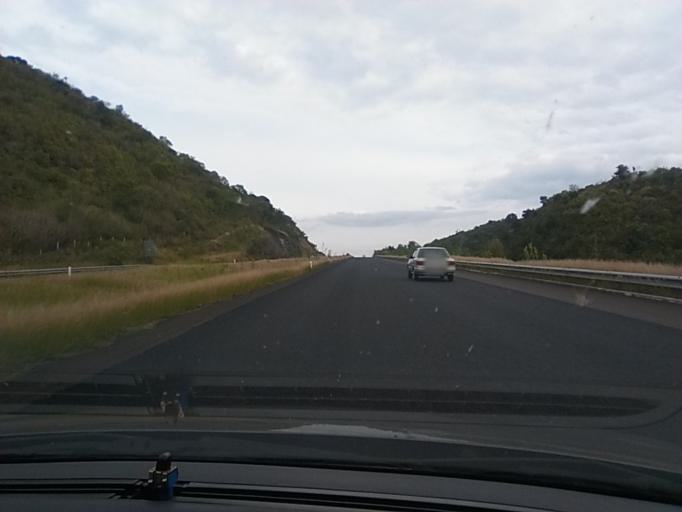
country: MX
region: Mexico
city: Huaniqueo de Morales
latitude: 19.8859
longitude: -101.4543
